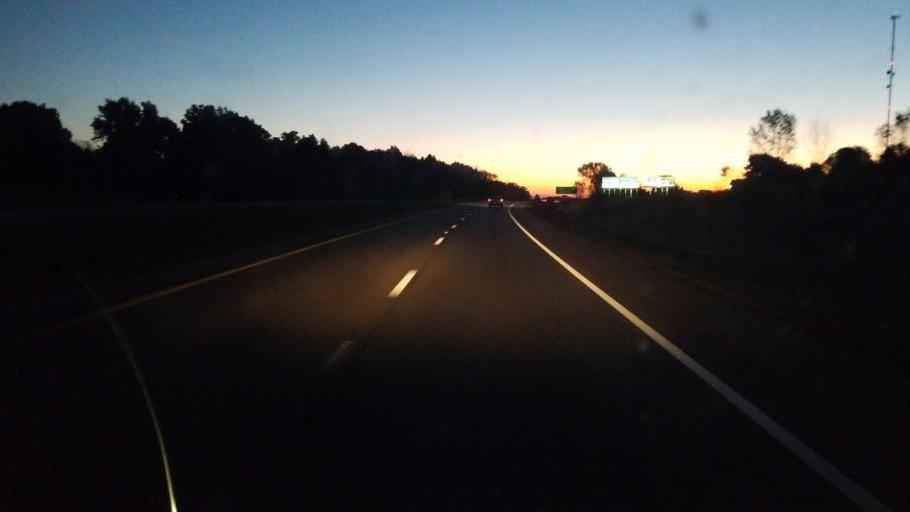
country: US
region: Ohio
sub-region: Wayne County
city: Wooster
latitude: 40.7988
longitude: -82.0343
